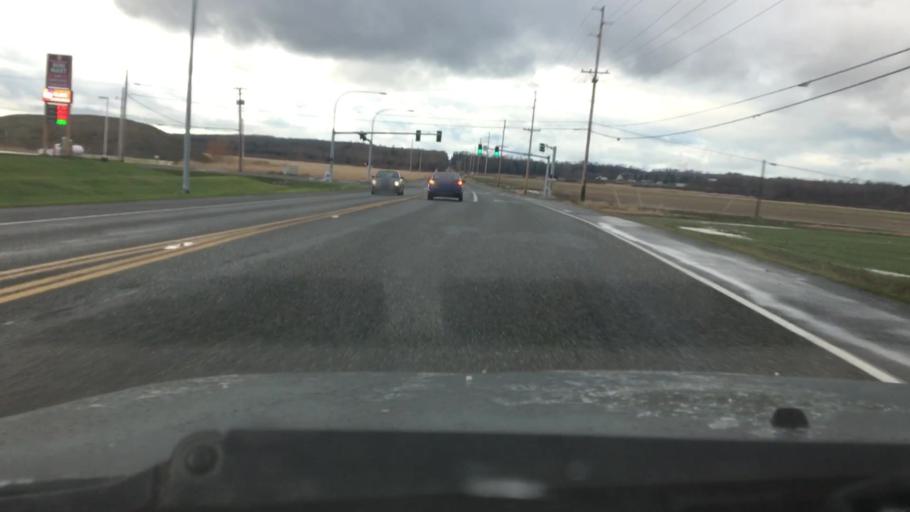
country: US
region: Washington
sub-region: Whatcom County
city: Ferndale
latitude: 48.8193
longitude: -122.6264
